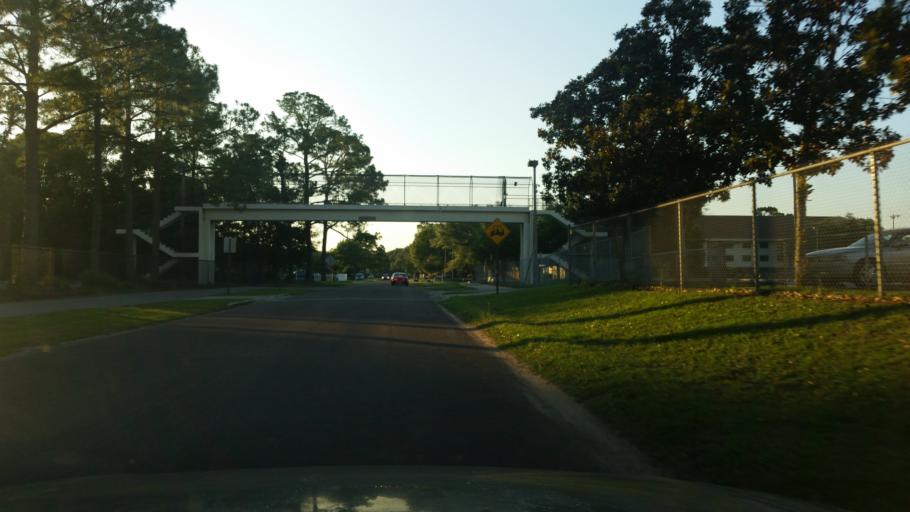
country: US
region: Florida
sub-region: Escambia County
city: Brent
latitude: 30.4760
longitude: -87.2326
